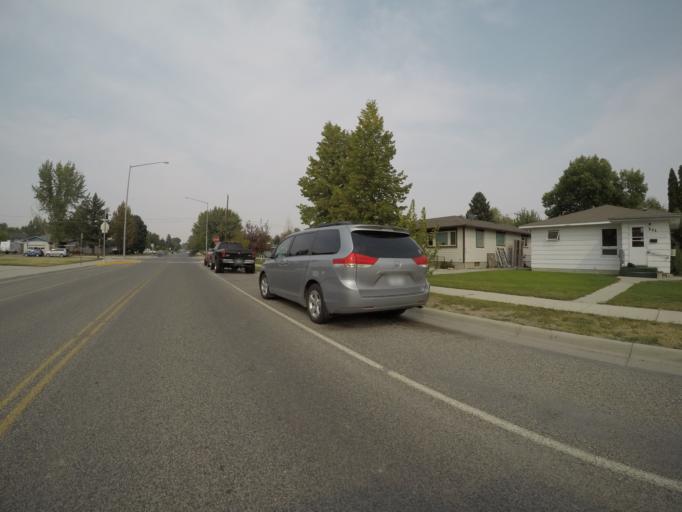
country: US
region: Montana
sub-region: Yellowstone County
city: Laurel
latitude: 45.6740
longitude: -108.7820
